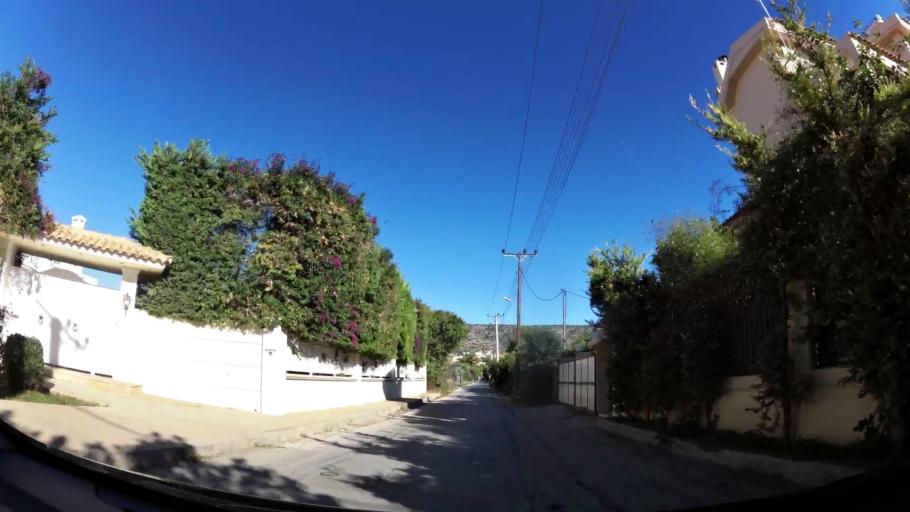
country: GR
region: Attica
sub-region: Nomarchia Anatolikis Attikis
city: Vari
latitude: 37.8336
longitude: 23.8163
